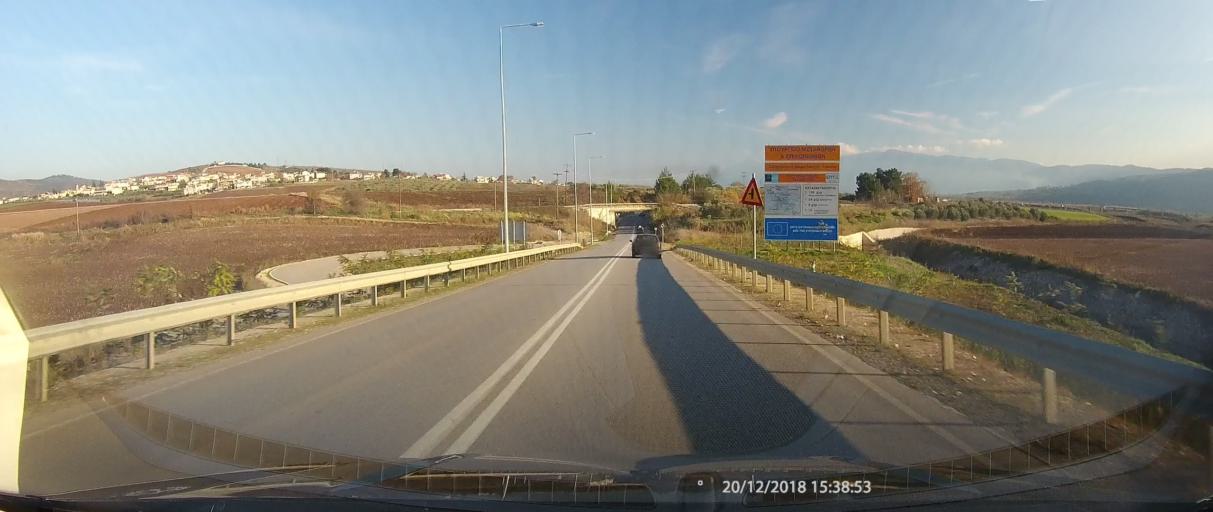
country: GR
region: Central Greece
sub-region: Nomos Fthiotidos
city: Stavros
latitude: 38.9005
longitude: 22.3573
